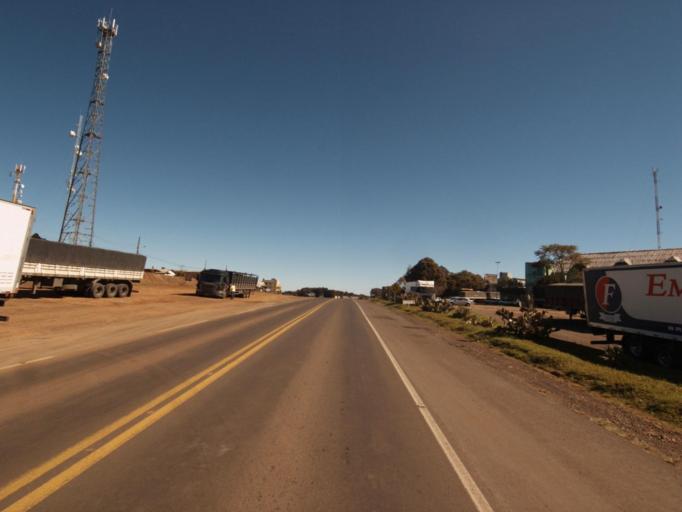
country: BR
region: Santa Catarina
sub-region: Xanxere
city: Xanxere
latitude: -26.8561
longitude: -52.2582
